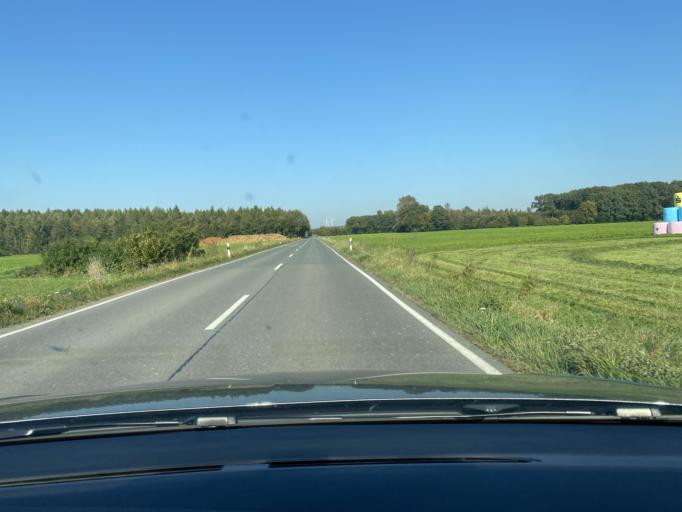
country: DE
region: North Rhine-Westphalia
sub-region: Regierungsbezirk Munster
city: Horstmar
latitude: 52.0521
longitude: 7.2773
